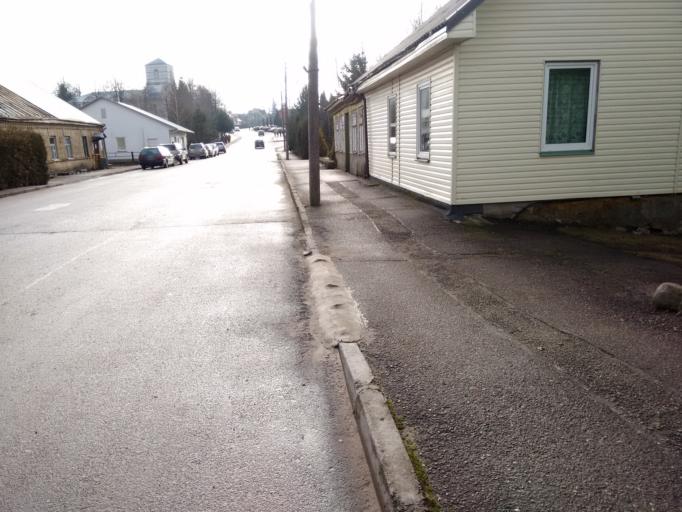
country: LT
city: Veisiejai
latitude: 54.2318
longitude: 23.8133
